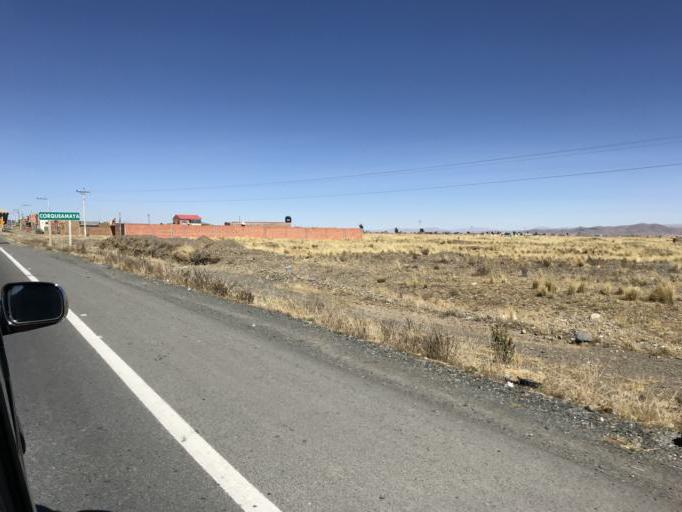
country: BO
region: La Paz
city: Batallas
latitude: -16.3257
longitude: -68.4271
